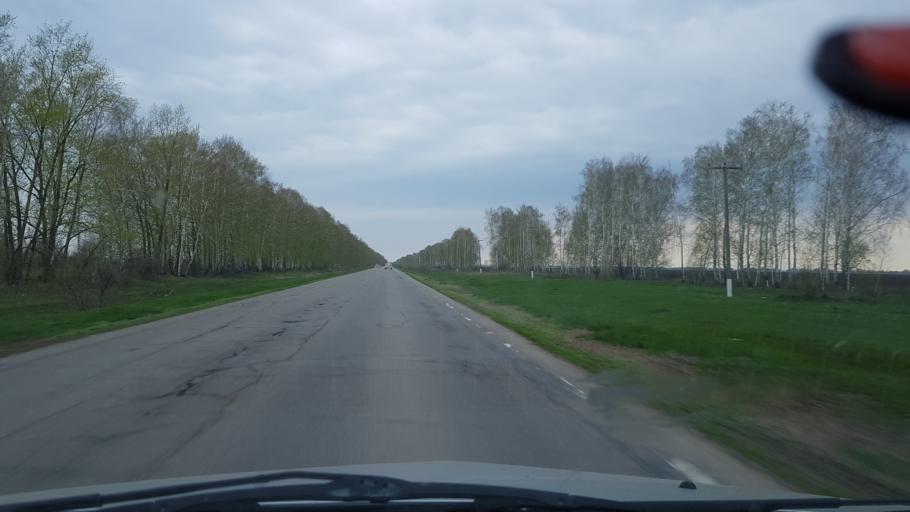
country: RU
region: Samara
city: Podstepki
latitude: 53.6595
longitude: 49.2294
